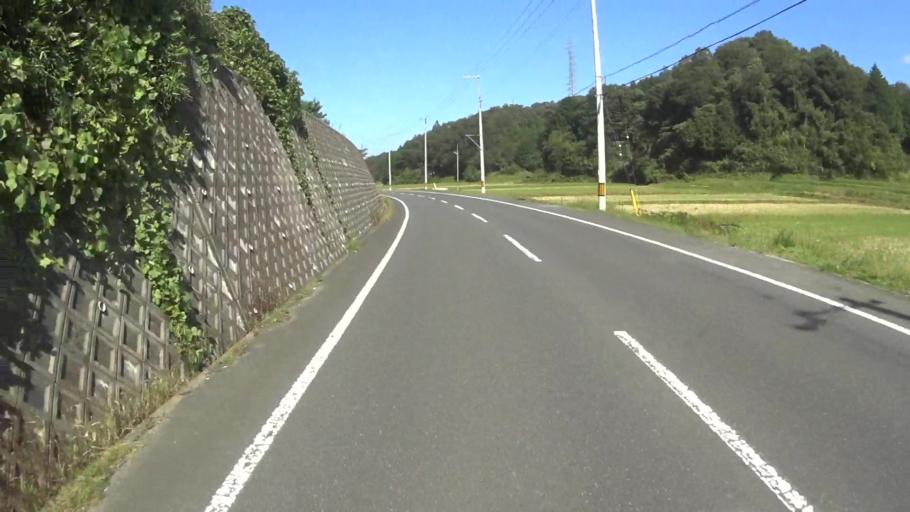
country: JP
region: Kyoto
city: Miyazu
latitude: 35.6657
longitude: 135.0598
